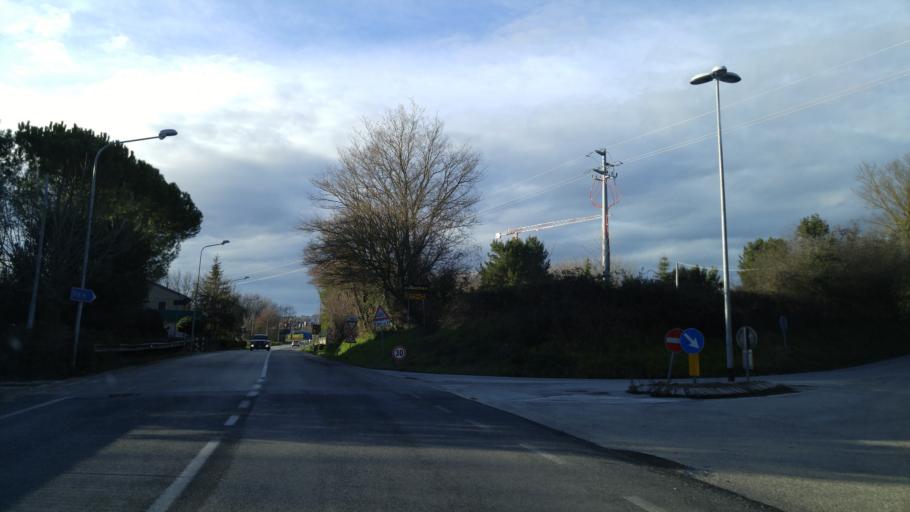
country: IT
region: The Marches
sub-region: Provincia di Ancona
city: Camerano
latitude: 43.5312
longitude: 13.5277
